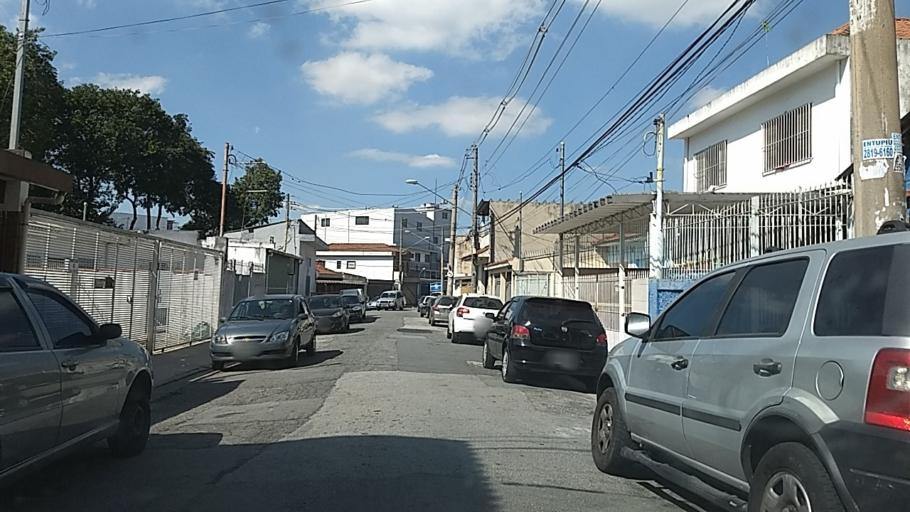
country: BR
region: Sao Paulo
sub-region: Guarulhos
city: Guarulhos
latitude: -23.4900
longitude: -46.5756
